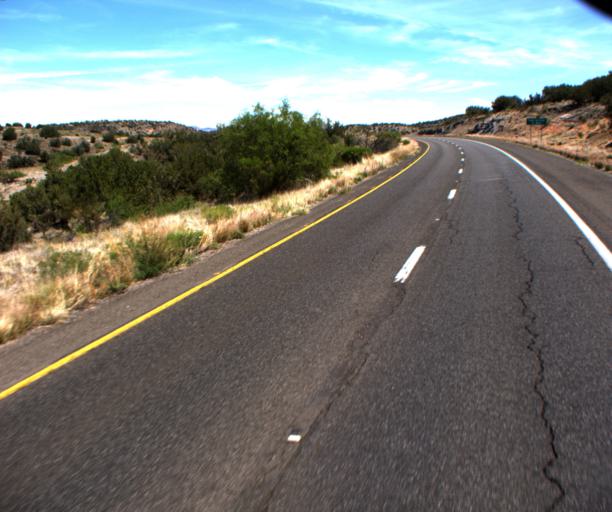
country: US
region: Arizona
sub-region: Yavapai County
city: Cornville
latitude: 34.7877
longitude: -111.9194
